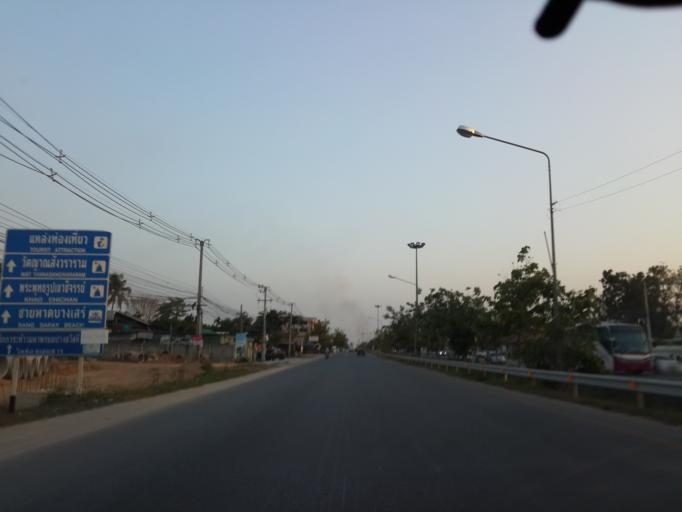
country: TH
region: Chon Buri
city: Phatthaya
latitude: 12.8347
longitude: 100.9131
